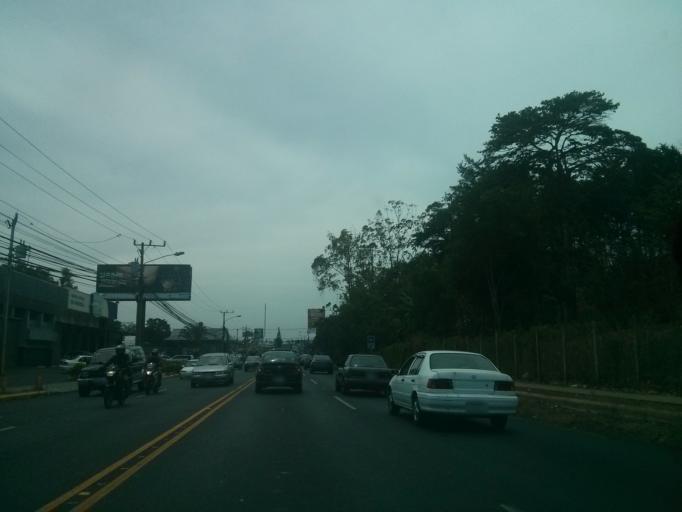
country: CR
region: San Jose
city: Curridabat
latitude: 9.9170
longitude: -84.0329
